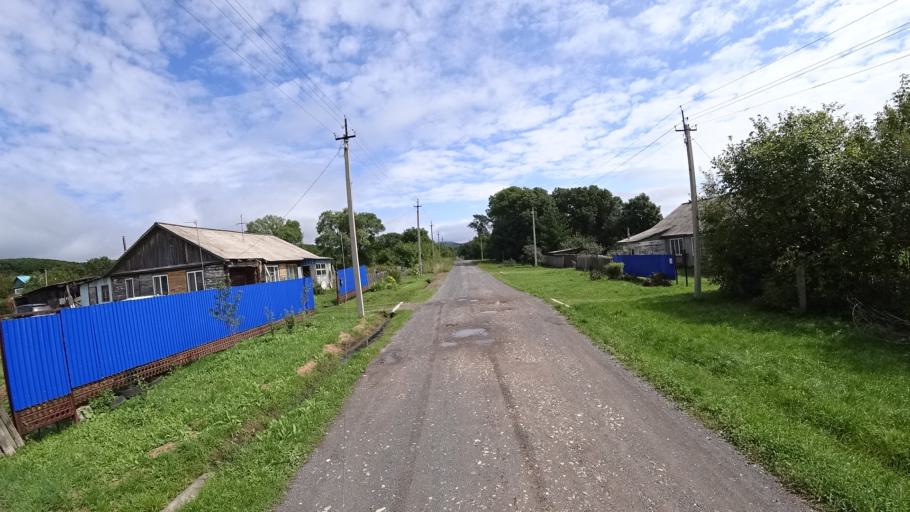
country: RU
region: Primorskiy
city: Lyalichi
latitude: 44.1400
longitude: 132.3774
